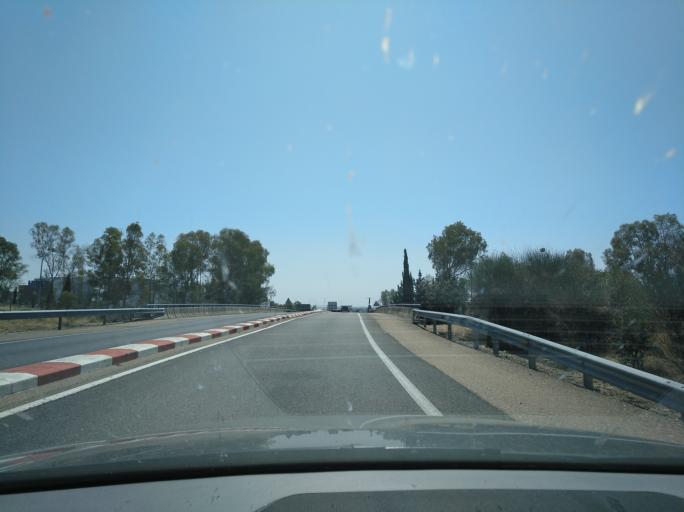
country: ES
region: Extremadura
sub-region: Provincia de Badajoz
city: Badajoz
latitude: 38.8860
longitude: -7.0261
